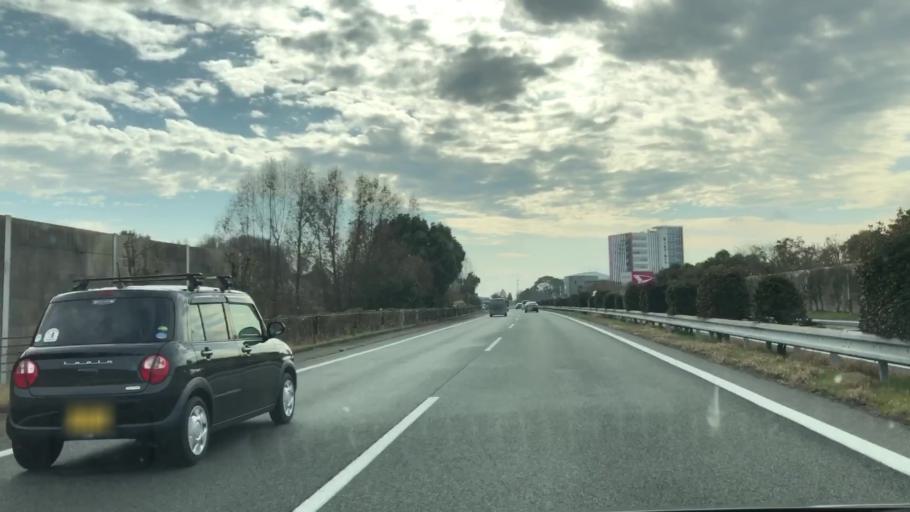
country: JP
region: Fukuoka
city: Kurume
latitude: 33.2696
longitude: 130.5399
